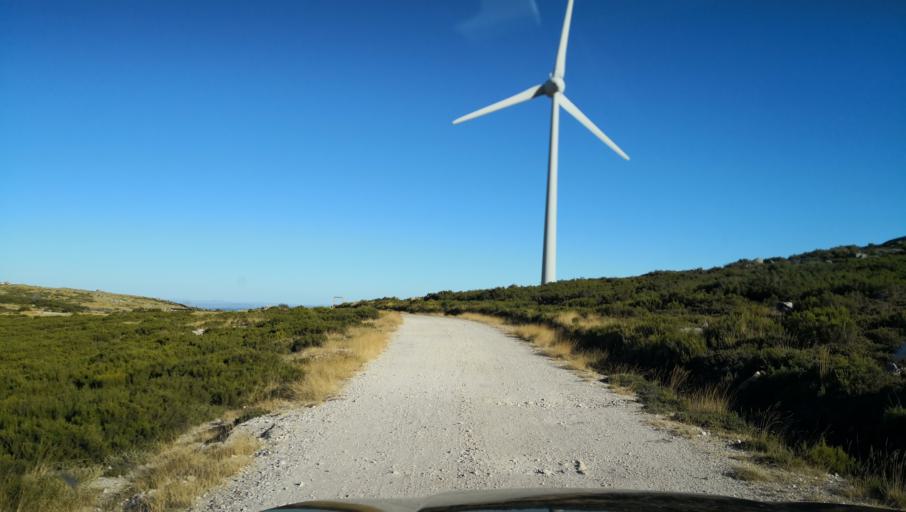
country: PT
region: Vila Real
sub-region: Vila Real
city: Vila Real
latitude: 41.3560
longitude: -7.7722
